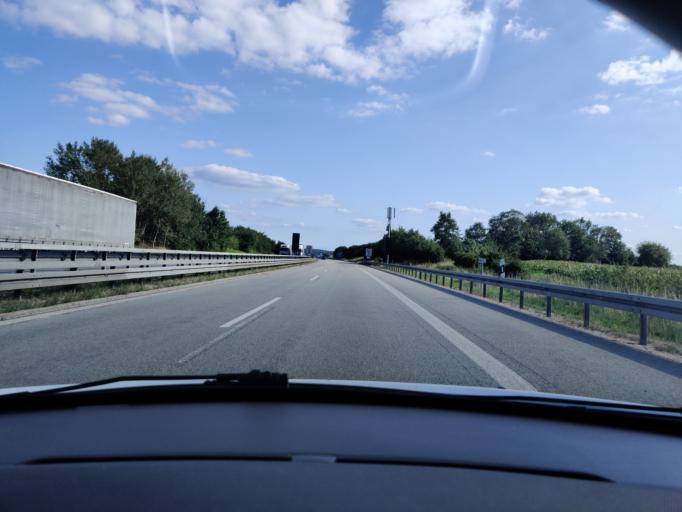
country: DE
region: Bavaria
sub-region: Upper Palatinate
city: Pfreimd
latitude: 49.4821
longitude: 12.1892
